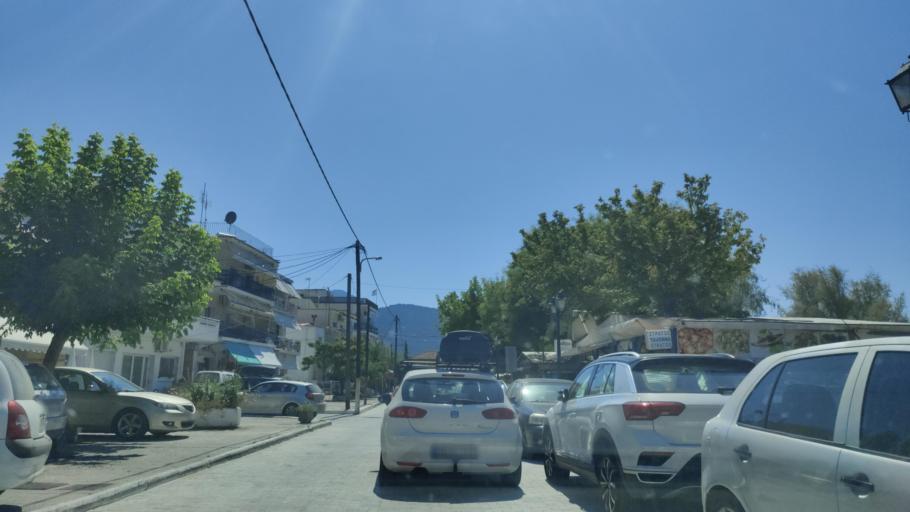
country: GR
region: East Macedonia and Thrace
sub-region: Nomos Kavalas
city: Thasos
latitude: 40.7826
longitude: 24.7147
